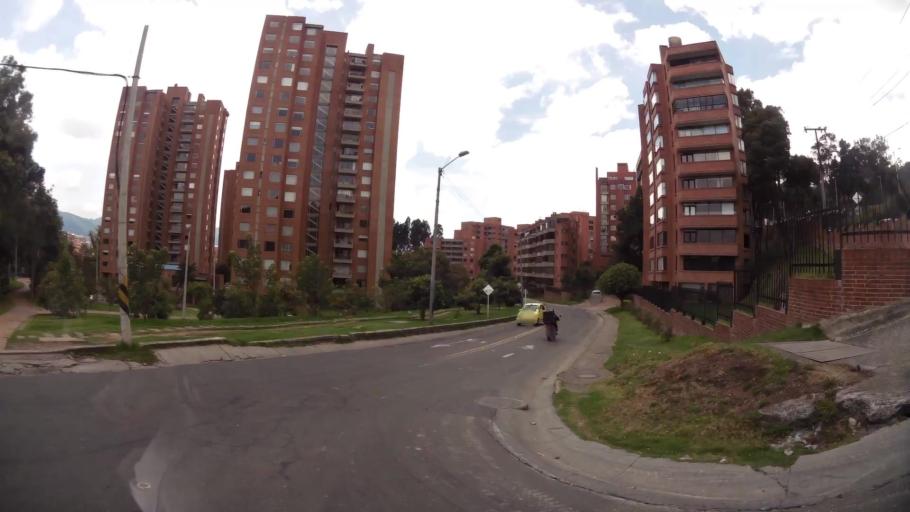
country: CO
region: Cundinamarca
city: Cota
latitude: 4.7333
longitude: -74.0742
